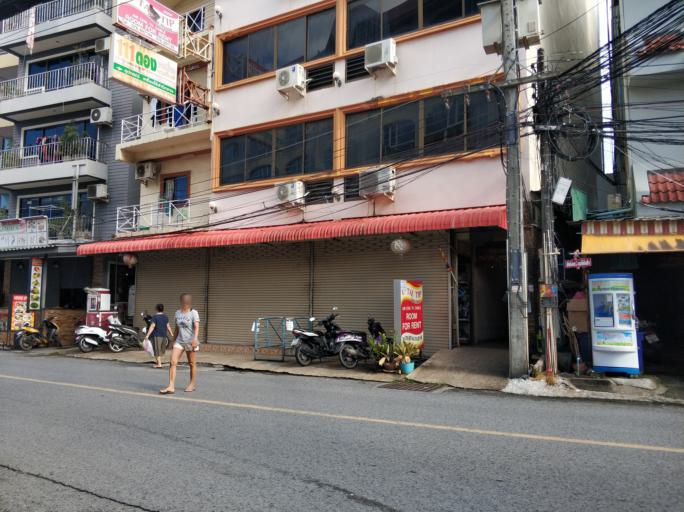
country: TH
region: Phuket
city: Patong
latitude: 7.8954
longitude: 98.3042
